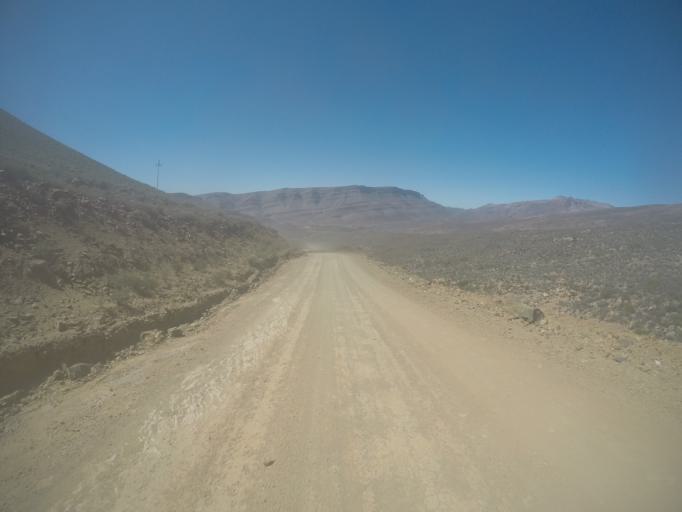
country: ZA
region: Western Cape
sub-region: West Coast District Municipality
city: Clanwilliam
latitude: -32.6163
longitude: 19.3755
